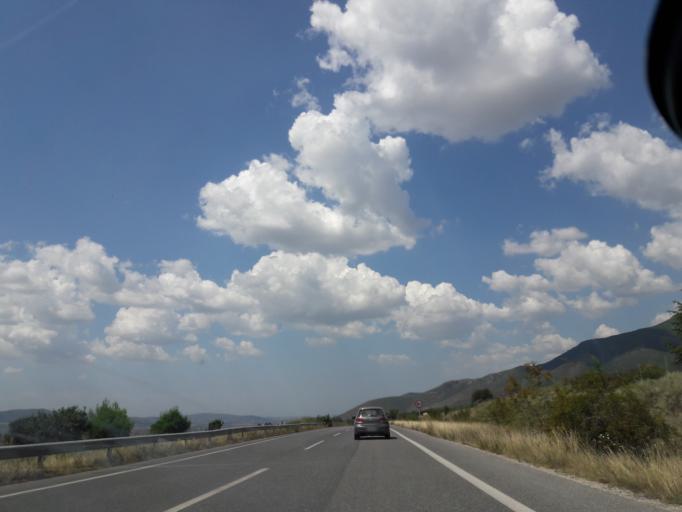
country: GR
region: Central Macedonia
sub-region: Nomos Chalkidikis
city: Galatista
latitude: 40.4654
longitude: 23.2593
